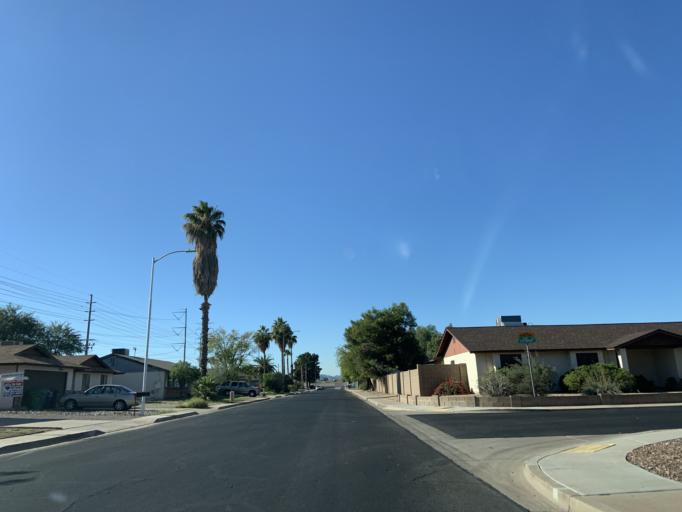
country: US
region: Arizona
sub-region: Maricopa County
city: San Carlos
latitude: 33.3575
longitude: -111.8646
